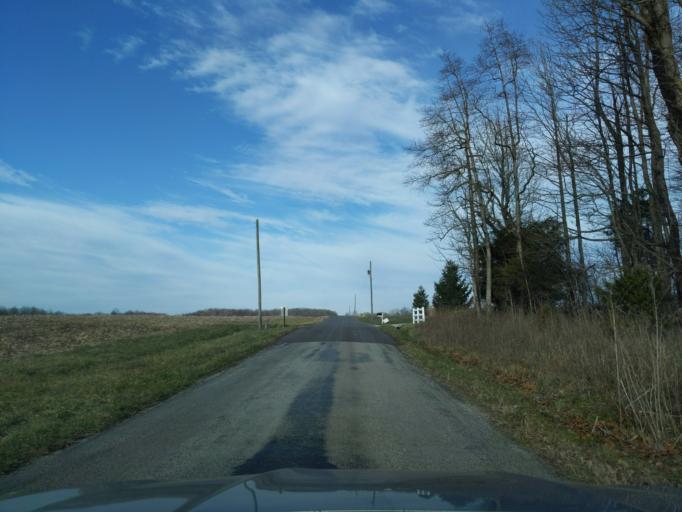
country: US
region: Indiana
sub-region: Decatur County
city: Greensburg
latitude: 39.2188
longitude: -85.4297
